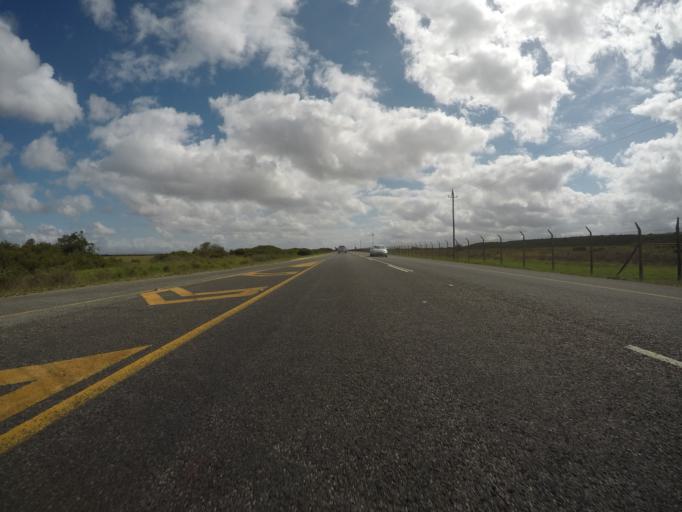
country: ZA
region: Western Cape
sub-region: Eden District Municipality
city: Mossel Bay
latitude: -34.1793
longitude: 21.9695
